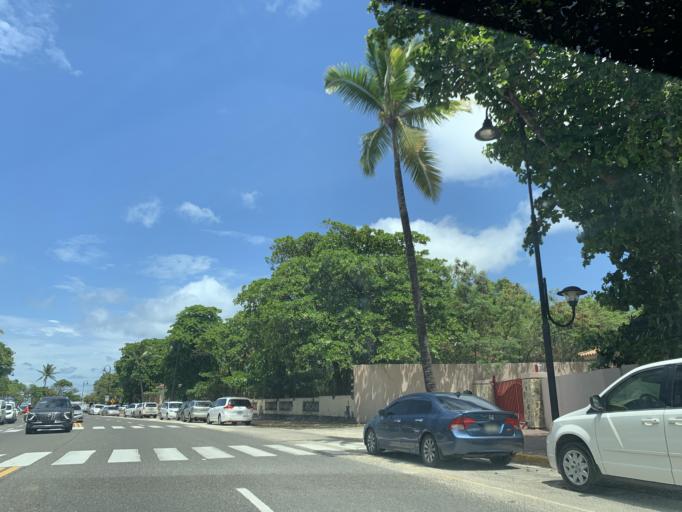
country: DO
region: Puerto Plata
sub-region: Puerto Plata
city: Puerto Plata
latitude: 19.7905
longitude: -70.6721
